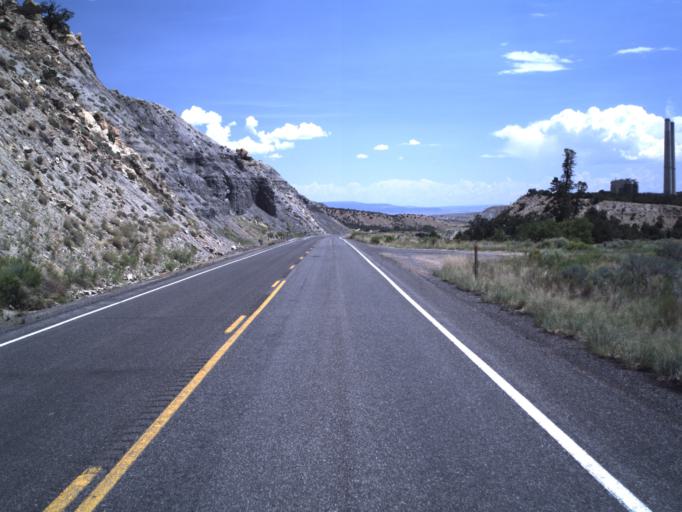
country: US
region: Utah
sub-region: Emery County
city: Huntington
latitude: 39.3919
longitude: -111.0931
